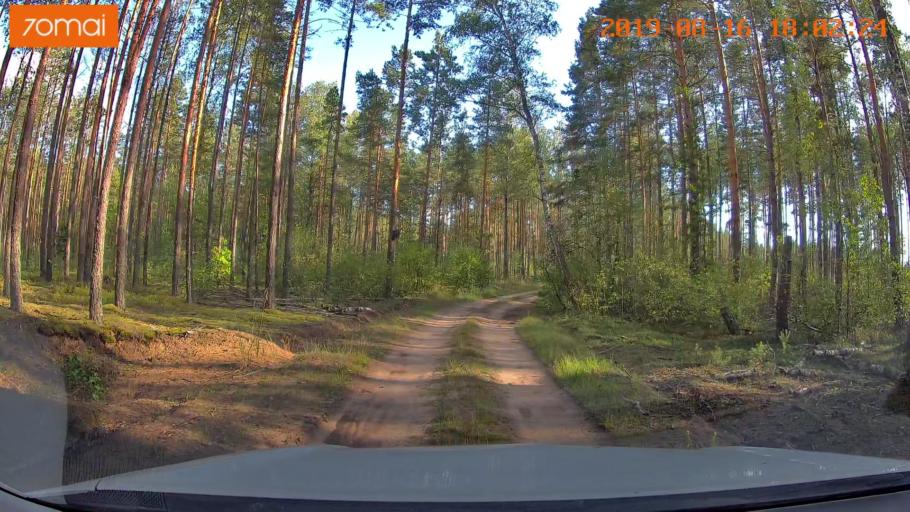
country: BY
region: Mogilev
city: Asipovichy
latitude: 53.2210
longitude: 28.6558
